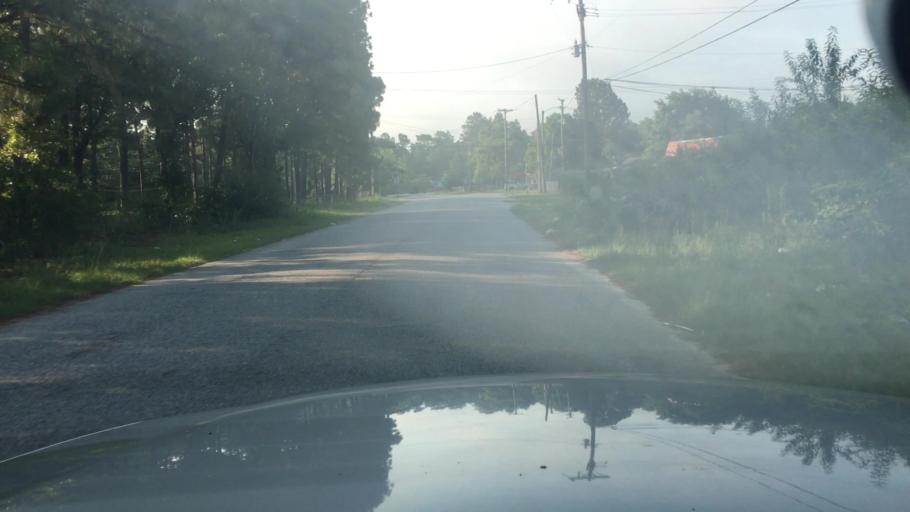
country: US
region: North Carolina
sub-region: Cumberland County
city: Spring Lake
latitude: 35.1112
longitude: -78.9356
